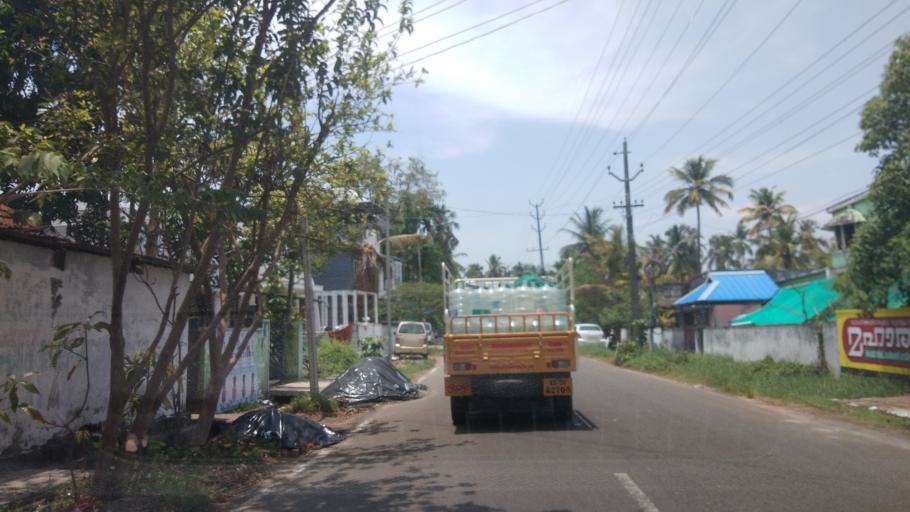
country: IN
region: Kerala
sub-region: Alappuzha
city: Kutiatodu
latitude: 9.8519
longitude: 76.2665
